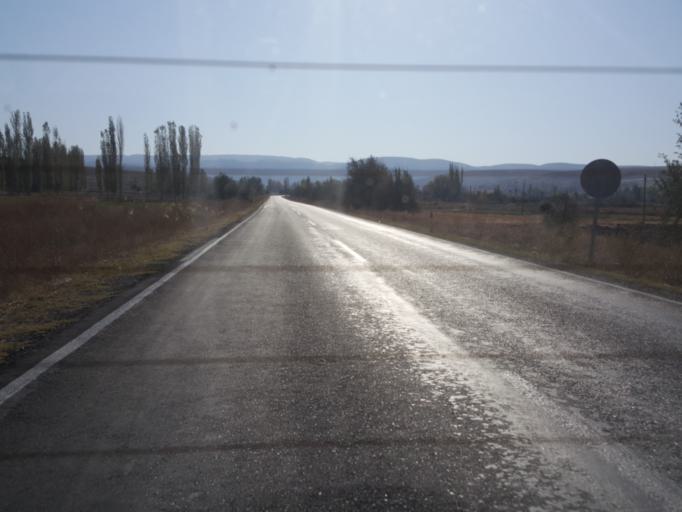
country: TR
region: Corum
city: Seydim
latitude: 40.5831
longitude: 34.6144
